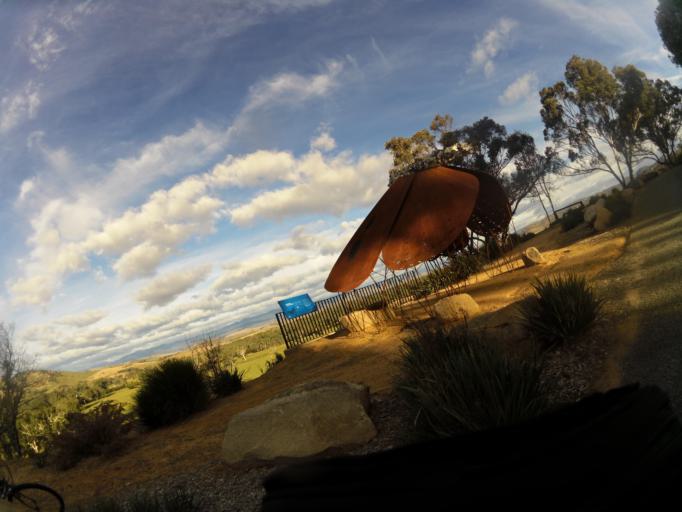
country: AU
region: New South Wales
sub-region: Greater Hume Shire
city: Holbrook
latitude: -36.0112
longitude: 147.9085
